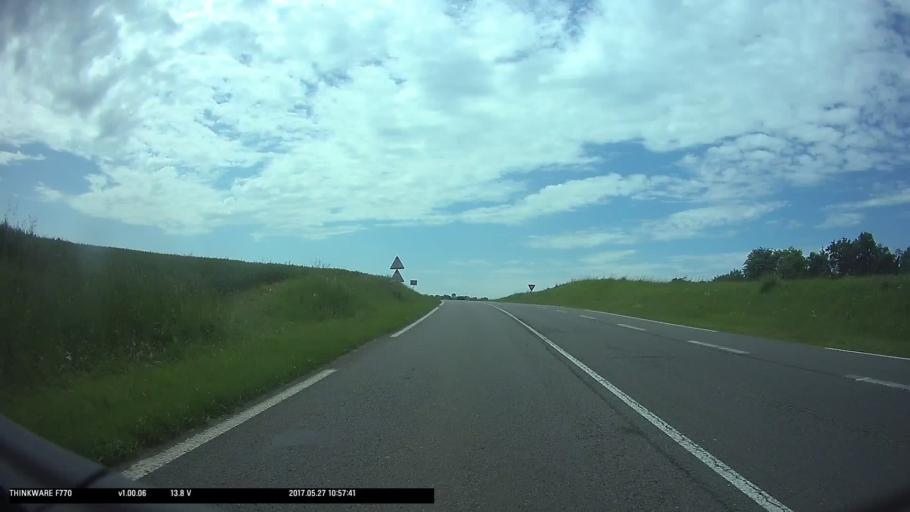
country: FR
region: Picardie
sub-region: Departement de l'Oise
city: Chaumont-en-Vexin
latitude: 49.2577
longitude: 1.8780
